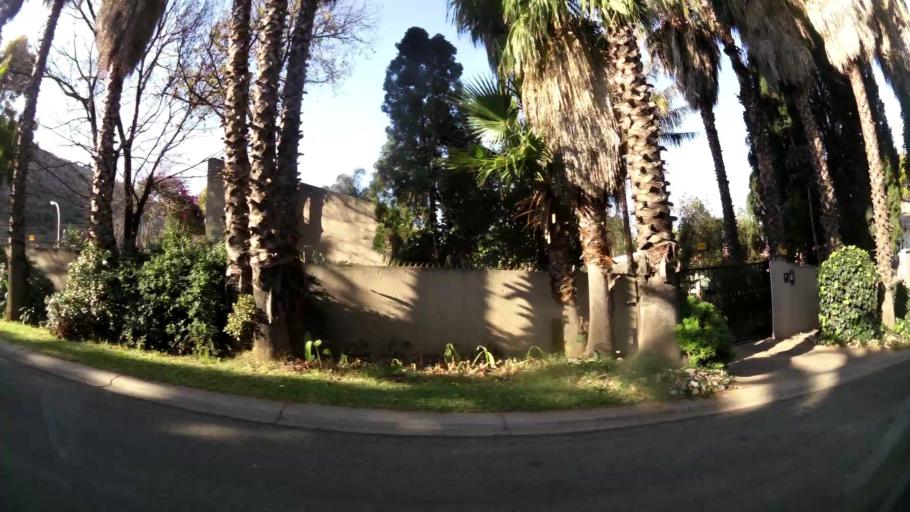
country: ZA
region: Gauteng
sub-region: City of Johannesburg Metropolitan Municipality
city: Johannesburg
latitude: -26.1695
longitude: 28.1167
